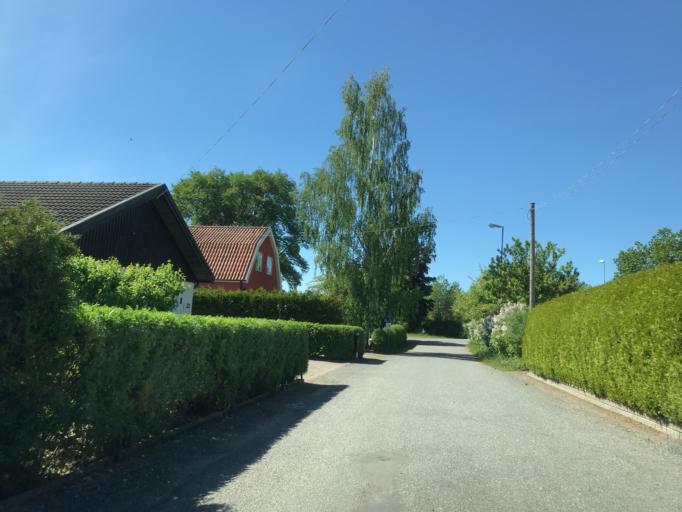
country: SE
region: Stockholm
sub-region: Sollentuna Kommun
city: Sollentuna
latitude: 59.4192
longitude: 17.9653
